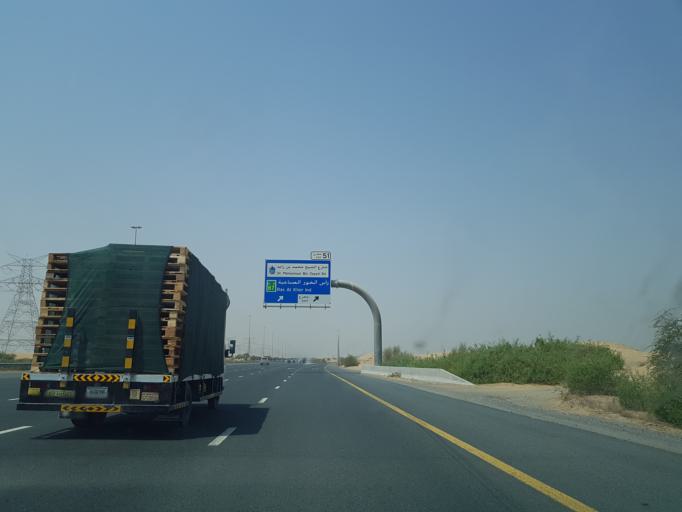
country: AE
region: Ash Shariqah
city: Sharjah
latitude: 25.1179
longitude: 55.4362
